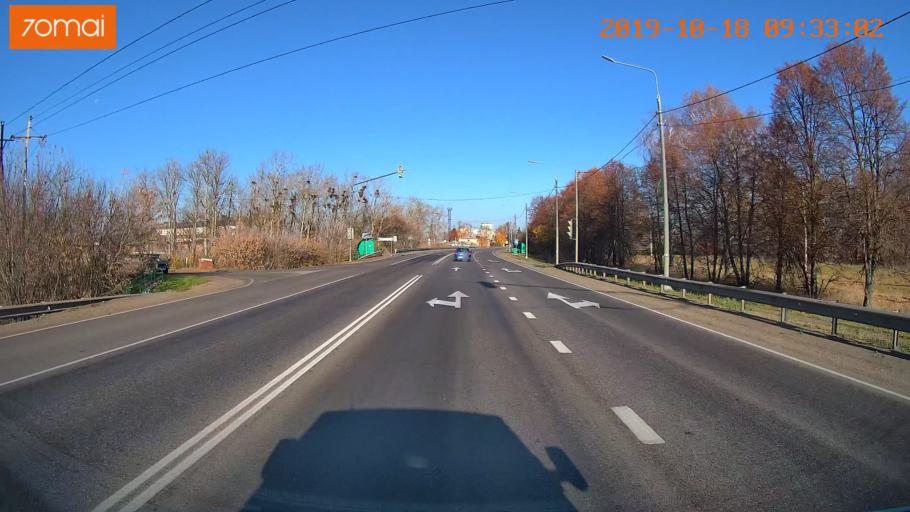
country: RU
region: Tula
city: Yefremov
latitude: 53.1628
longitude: 38.1535
